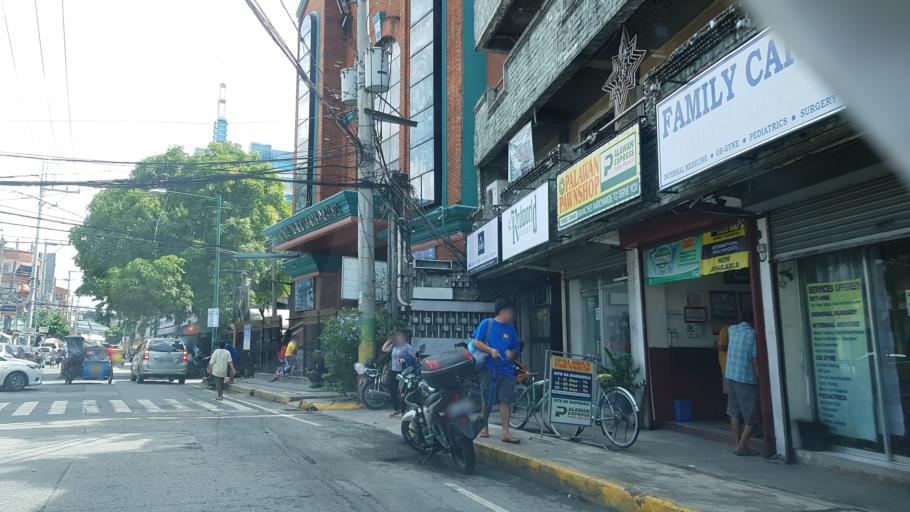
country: PH
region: Calabarzon
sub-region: Province of Rizal
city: Pateros
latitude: 14.5456
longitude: 121.0612
